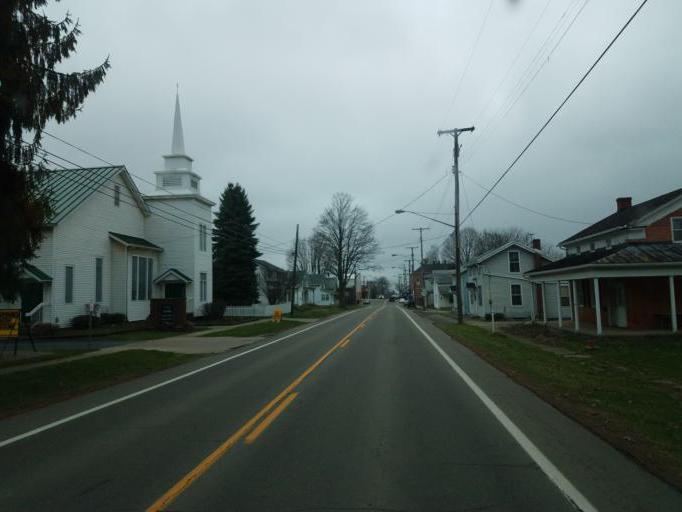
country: US
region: Ohio
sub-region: Ashland County
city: Ashland
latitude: 40.7714
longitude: -82.2621
